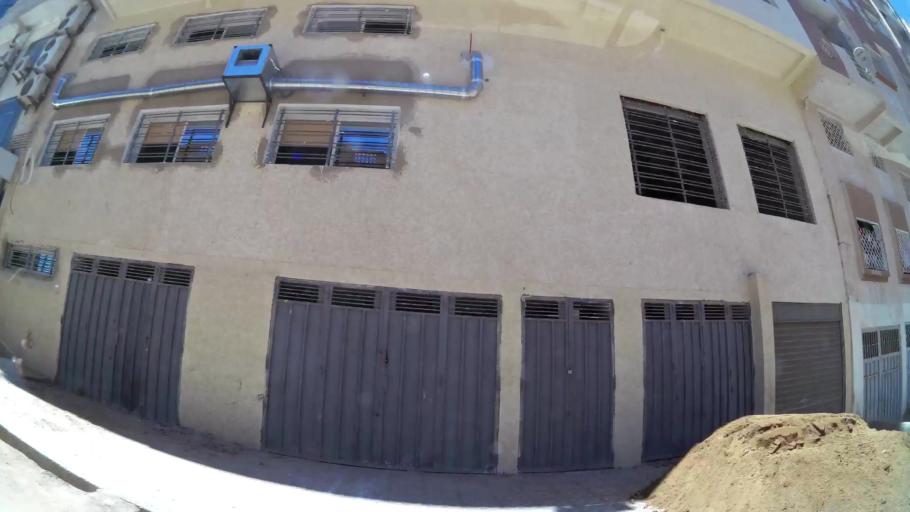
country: MA
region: Meknes-Tafilalet
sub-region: Meknes
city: Meknes
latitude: 33.8654
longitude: -5.5761
